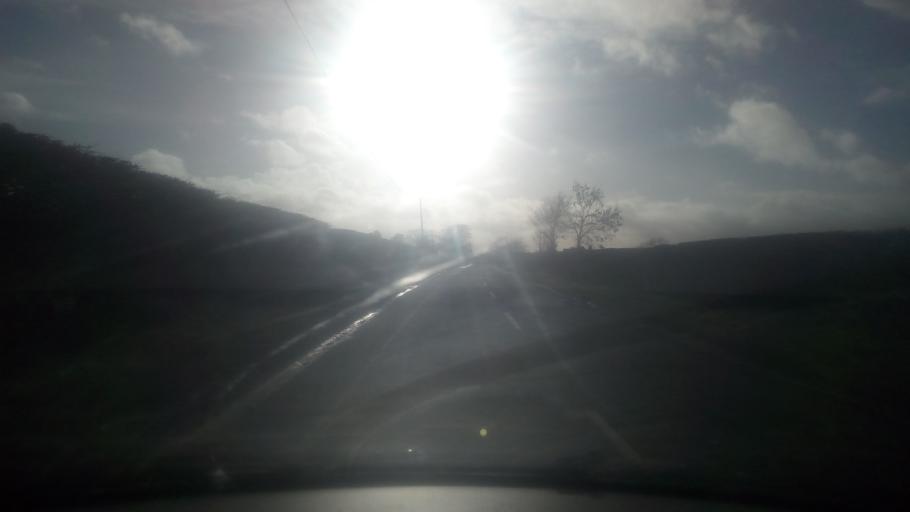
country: GB
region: Scotland
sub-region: The Scottish Borders
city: Coldstream
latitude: 55.7158
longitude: -2.2762
